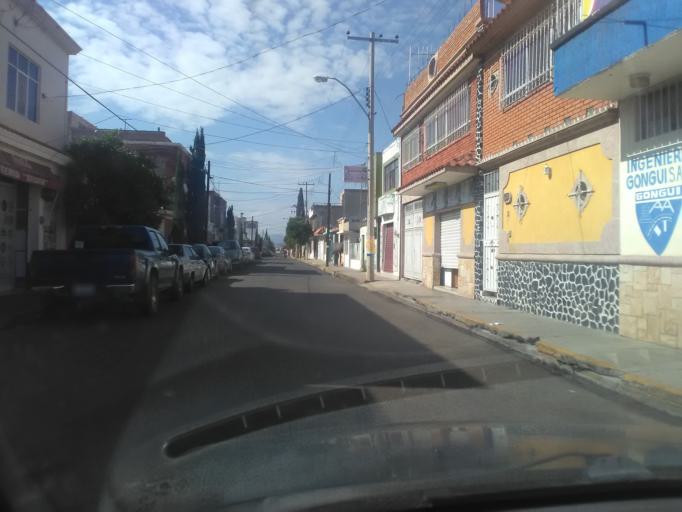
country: MX
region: Durango
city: Victoria de Durango
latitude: 24.0239
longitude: -104.6581
